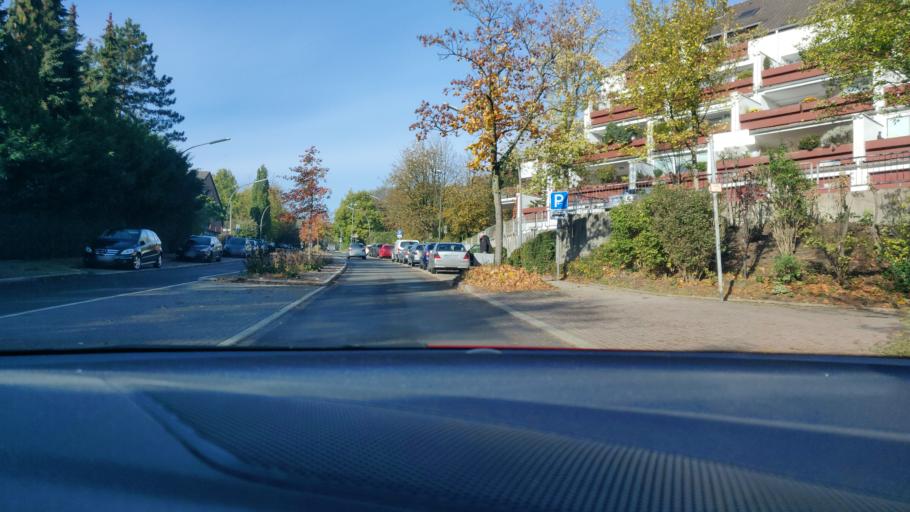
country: DE
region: North Rhine-Westphalia
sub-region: Regierungsbezirk Dusseldorf
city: Velbert
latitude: 51.3486
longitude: 7.0193
